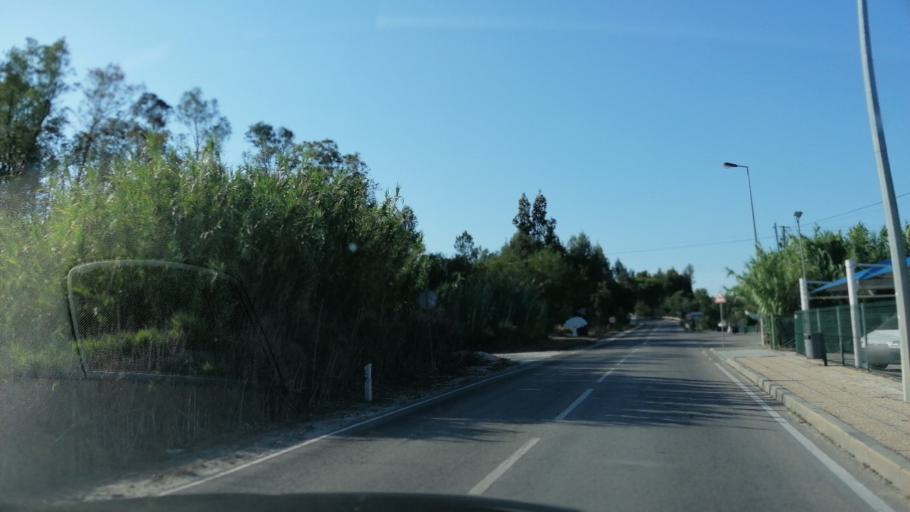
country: PT
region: Santarem
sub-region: Coruche
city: Coruche
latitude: 38.9690
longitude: -8.5362
